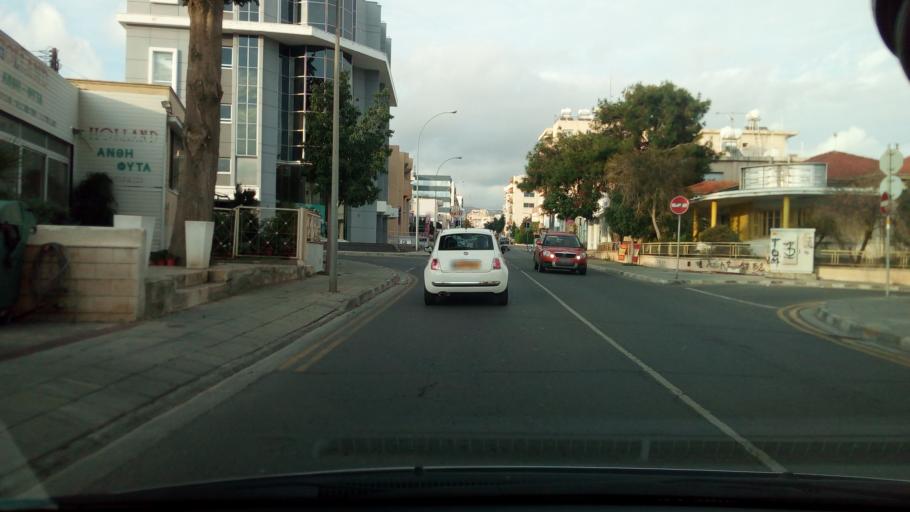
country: CY
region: Limassol
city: Limassol
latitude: 34.6903
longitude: 33.0446
